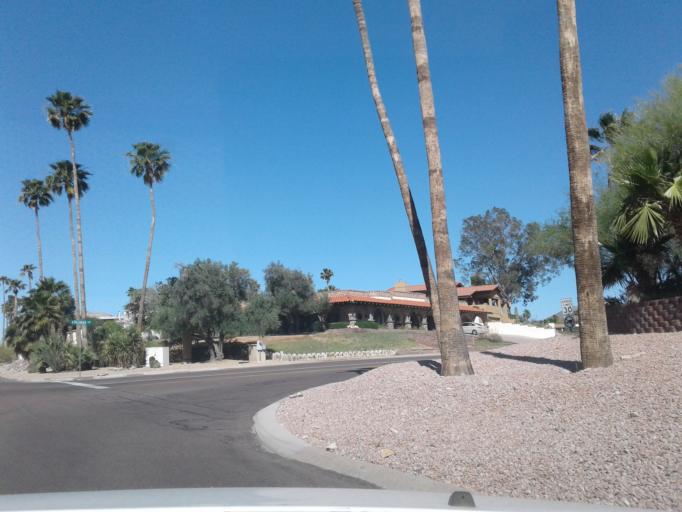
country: US
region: Arizona
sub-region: Maricopa County
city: Fountain Hills
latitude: 33.5870
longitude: -111.7367
